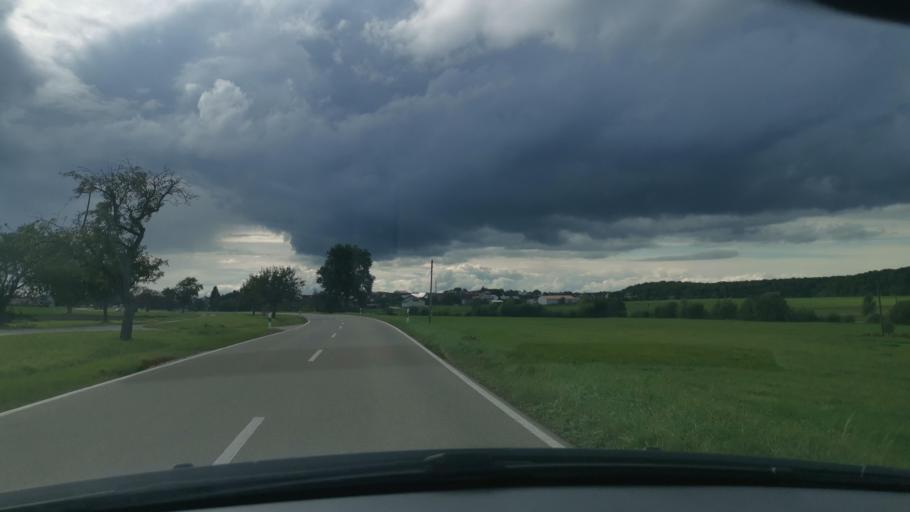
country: DE
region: Baden-Wuerttemberg
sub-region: Tuebingen Region
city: Lauterach
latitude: 48.3105
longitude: 9.6269
